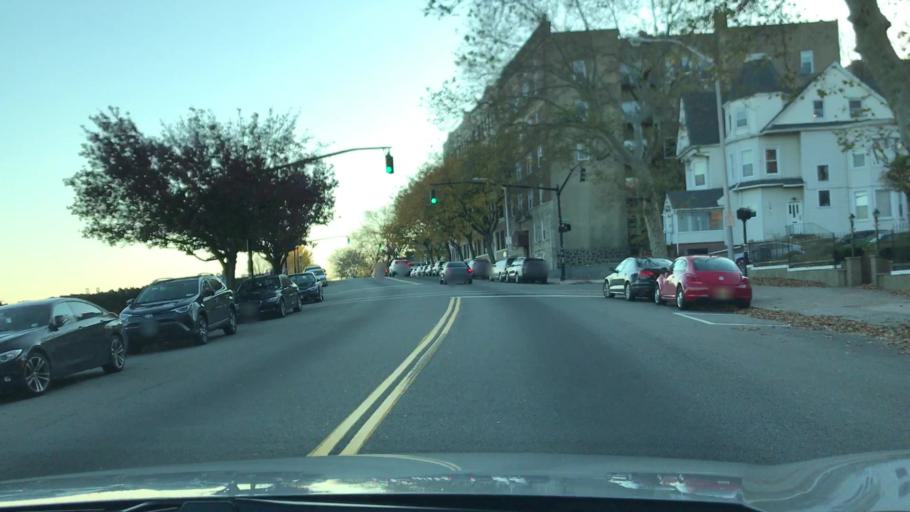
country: US
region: New Jersey
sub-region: Hudson County
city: Weehawken
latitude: 40.7742
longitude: -74.0151
